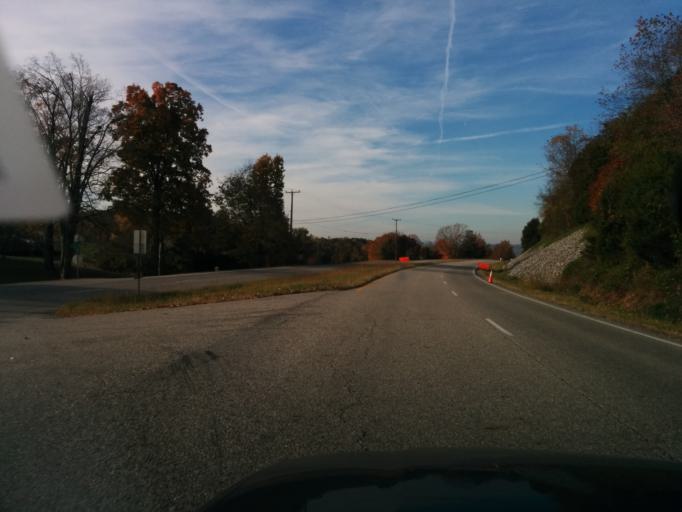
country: US
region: Virginia
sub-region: Rockbridge County
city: East Lexington
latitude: 37.8459
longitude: -79.3526
